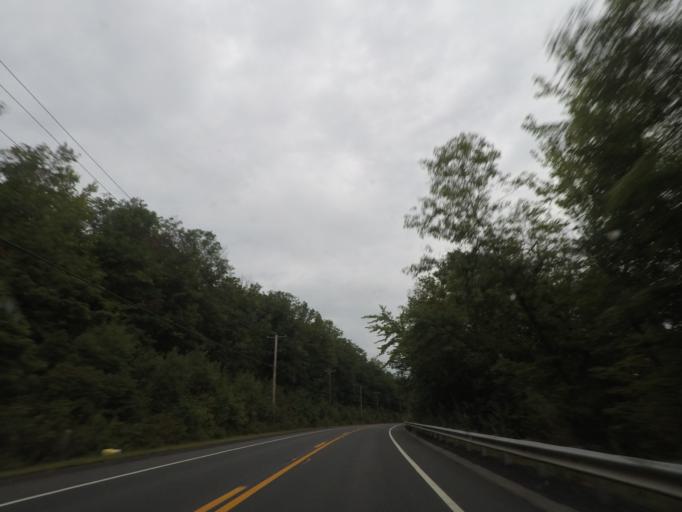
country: US
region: Massachusetts
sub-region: Hampshire County
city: Ware
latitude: 42.2048
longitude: -72.2621
